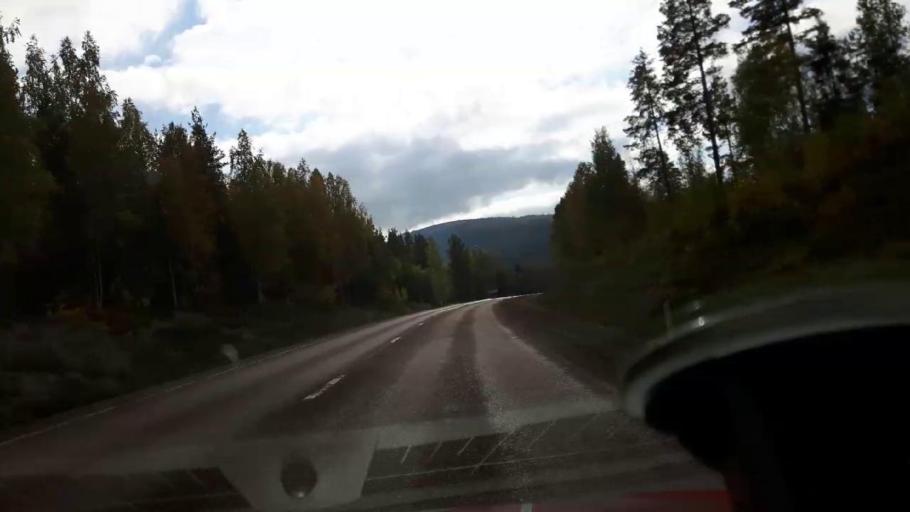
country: SE
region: Gaevleborg
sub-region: Bollnas Kommun
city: Arbra
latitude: 61.5833
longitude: 16.3156
